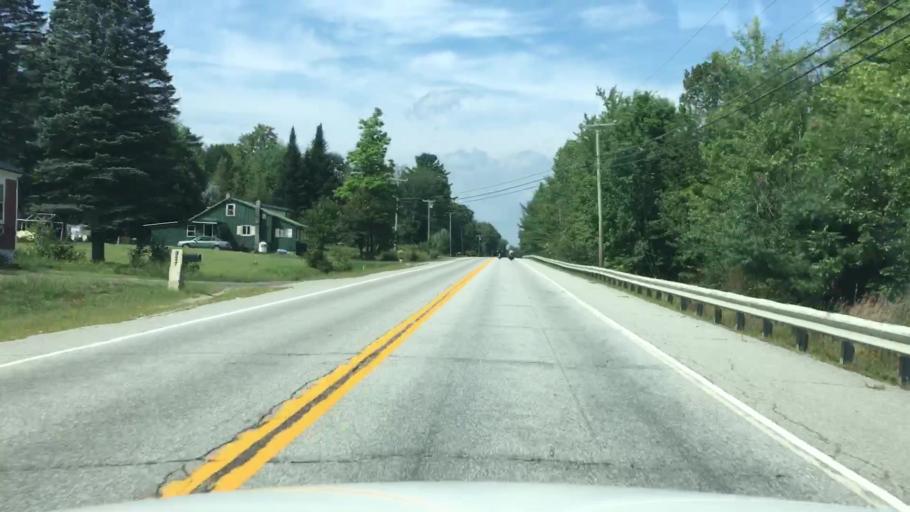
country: US
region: Maine
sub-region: Oxford County
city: Peru
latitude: 44.4954
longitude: -70.3892
